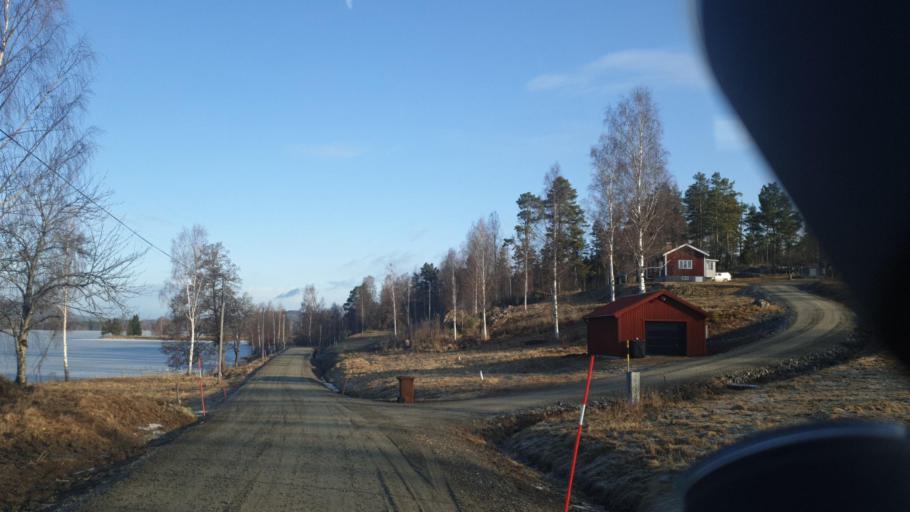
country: SE
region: Vaermland
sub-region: Arvika Kommun
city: Arvika
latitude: 59.7231
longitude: 12.8372
